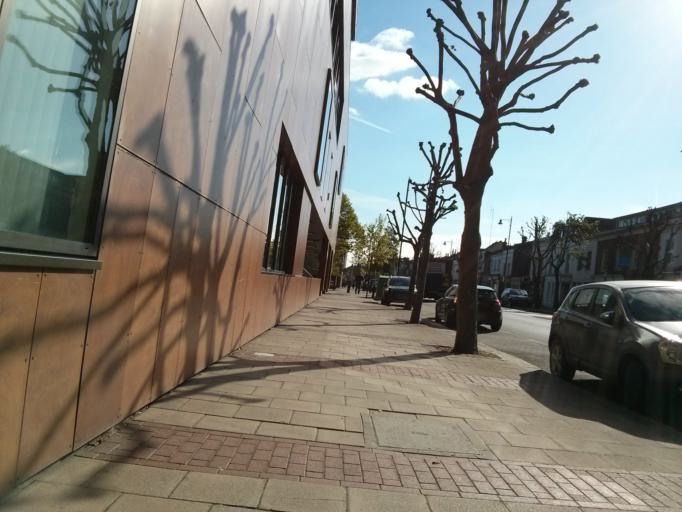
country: GB
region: England
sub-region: Greater London
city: Earlsfield
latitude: 51.4598
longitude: -0.1796
